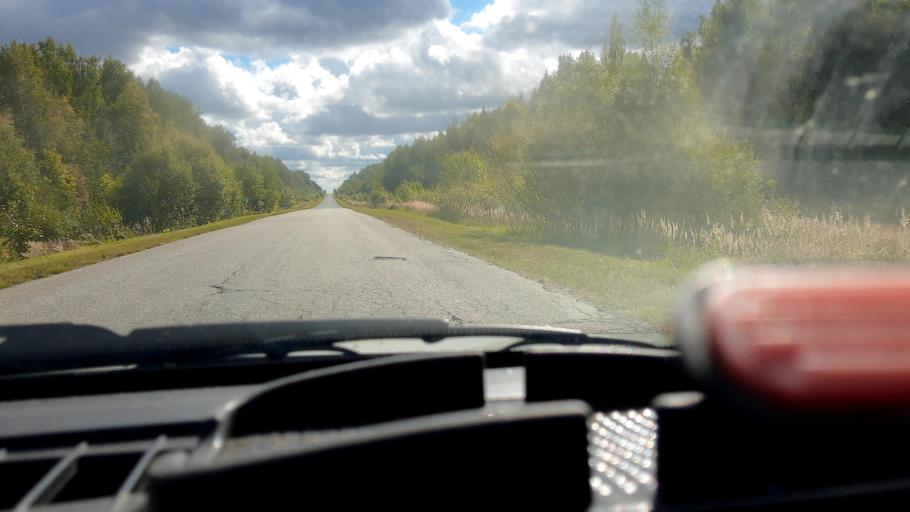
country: RU
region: Mariy-El
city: Kilemary
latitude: 56.9306
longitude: 46.7022
